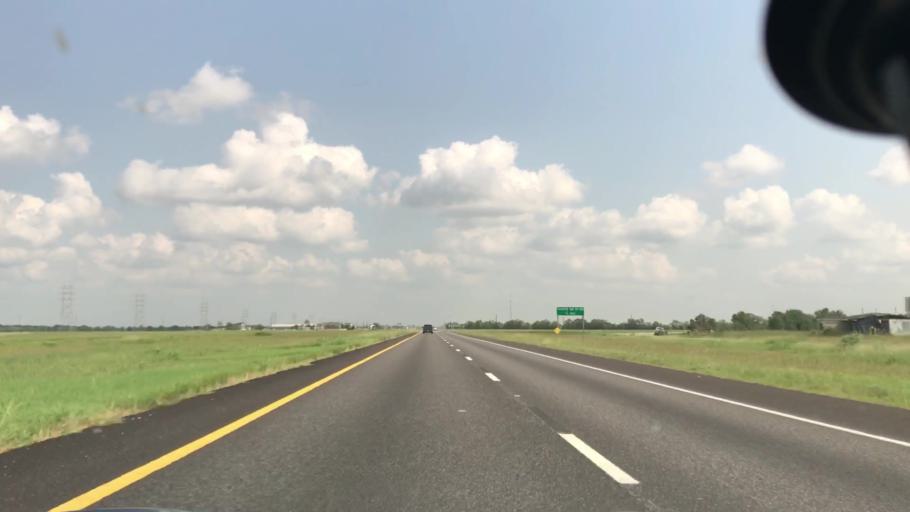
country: US
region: Texas
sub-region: Brazoria County
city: Rosharon
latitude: 29.4065
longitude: -95.4269
